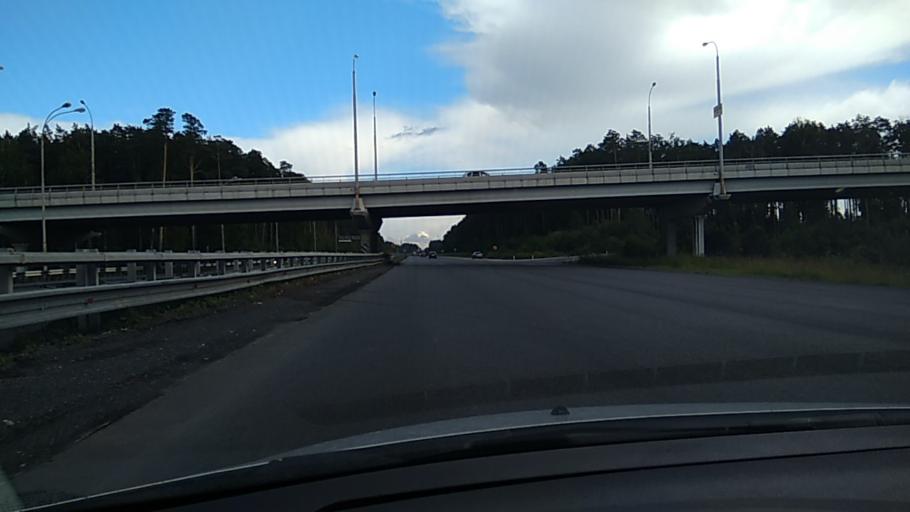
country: RU
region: Sverdlovsk
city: Shuvakish
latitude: 56.8935
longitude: 60.5337
